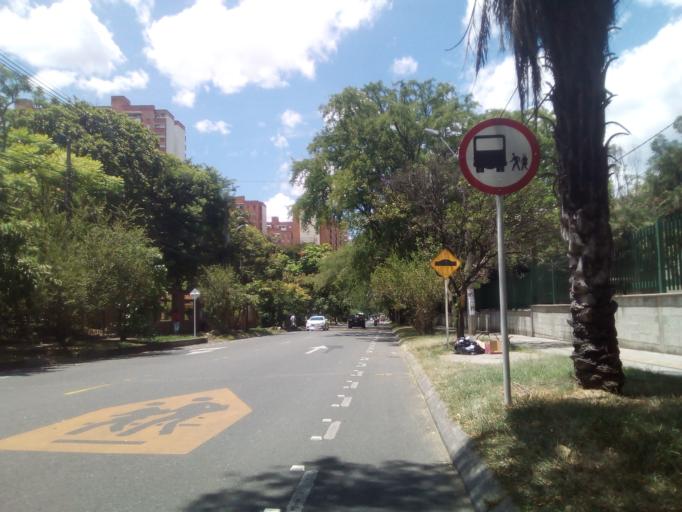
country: CO
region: Antioquia
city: Medellin
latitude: 6.2650
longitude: -75.5919
